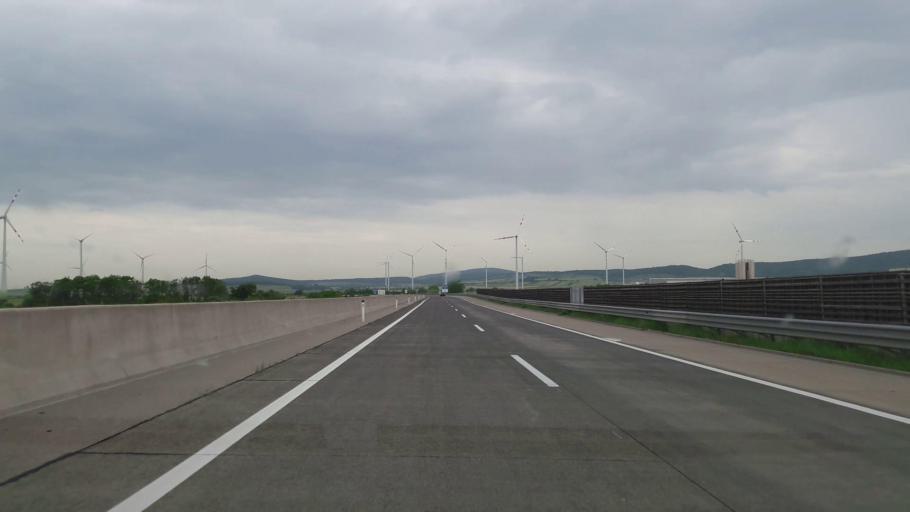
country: AT
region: Burgenland
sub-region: Politischer Bezirk Neusiedl am See
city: Kittsee
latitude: 48.0789
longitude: 17.0499
